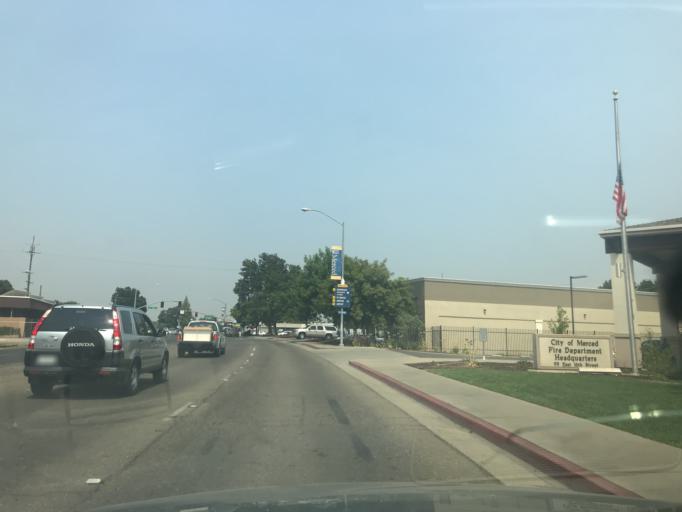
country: US
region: California
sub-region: Merced County
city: Merced
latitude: 37.2970
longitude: -120.4749
